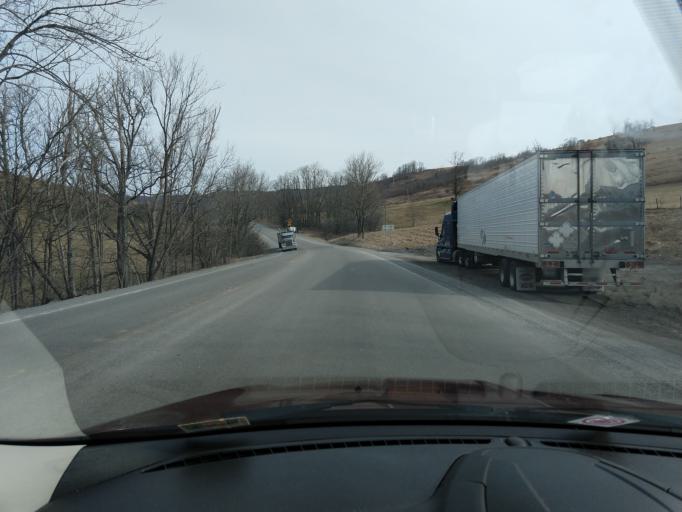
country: US
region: West Virginia
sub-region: Pendleton County
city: Franklin
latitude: 38.8896
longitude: -79.4681
